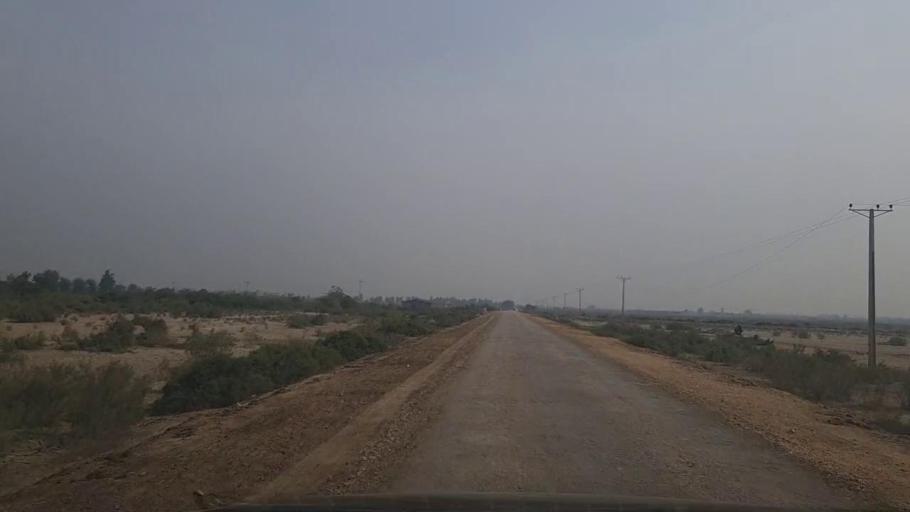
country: PK
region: Sindh
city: Mirpur Sakro
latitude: 24.4583
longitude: 67.6991
